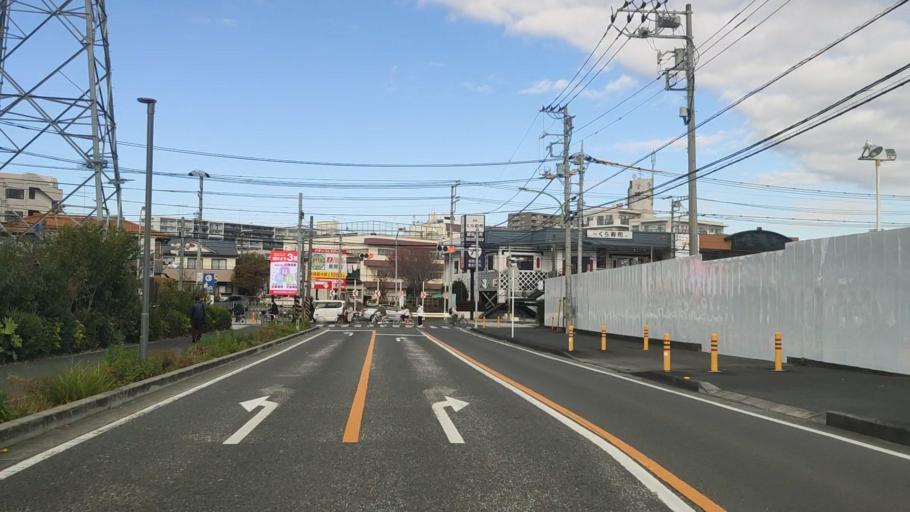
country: JP
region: Kanagawa
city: Minami-rinkan
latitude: 35.5014
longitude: 139.4266
